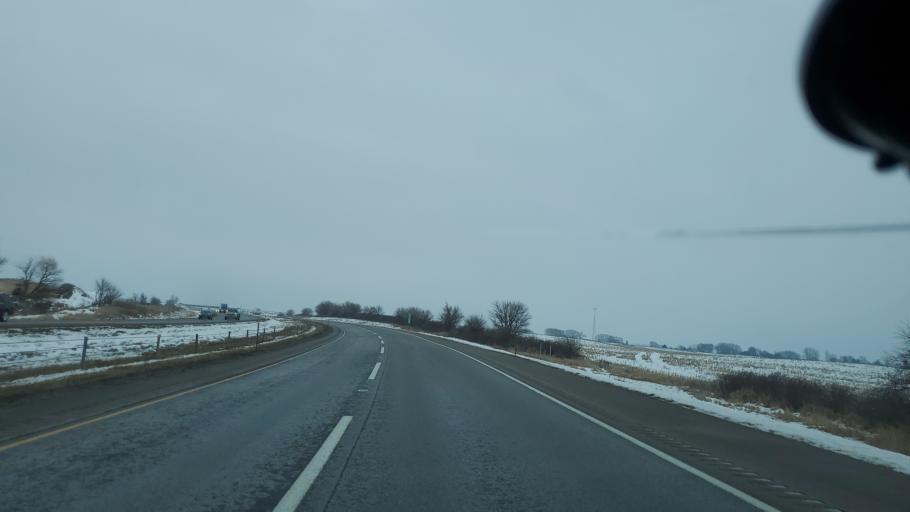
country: US
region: Illinois
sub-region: Kane County
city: Maple Park
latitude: 41.8757
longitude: -88.6136
